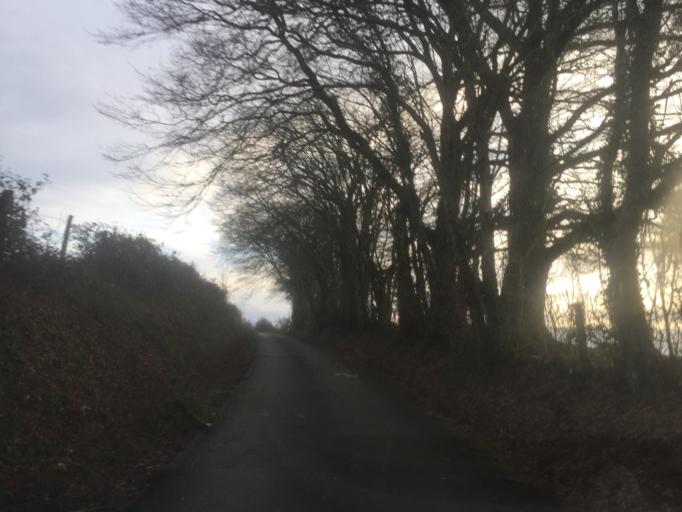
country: FR
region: Franche-Comte
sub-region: Departement du Jura
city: Orchamps
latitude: 47.1300
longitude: 5.6753
